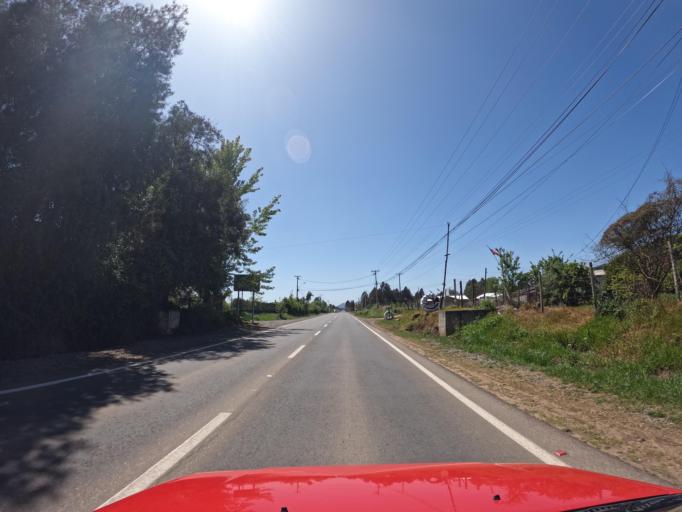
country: CL
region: Maule
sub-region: Provincia de Linares
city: Colbun
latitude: -35.7259
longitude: -71.4181
